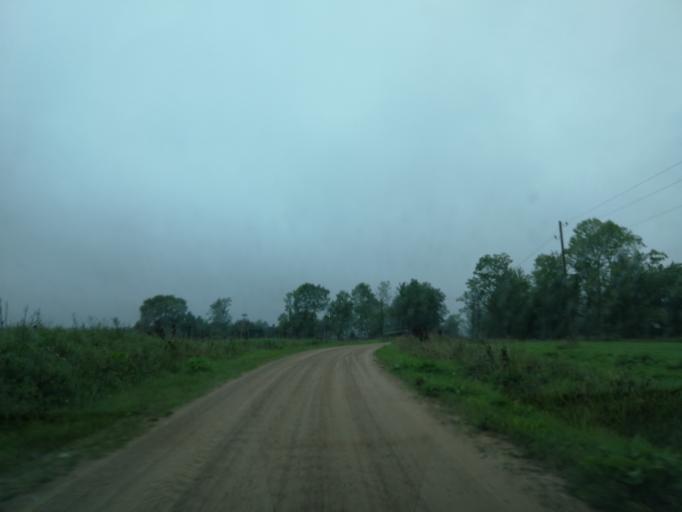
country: LV
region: Preilu Rajons
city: Jaunaglona
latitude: 56.3215
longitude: 27.0244
